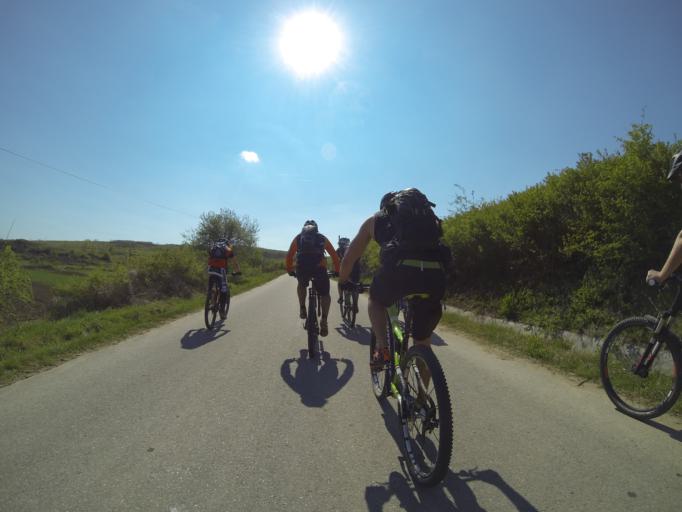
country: RO
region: Gorj
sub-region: Comuna Crusetu
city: Crusetu
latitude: 44.6188
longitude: 23.6671
